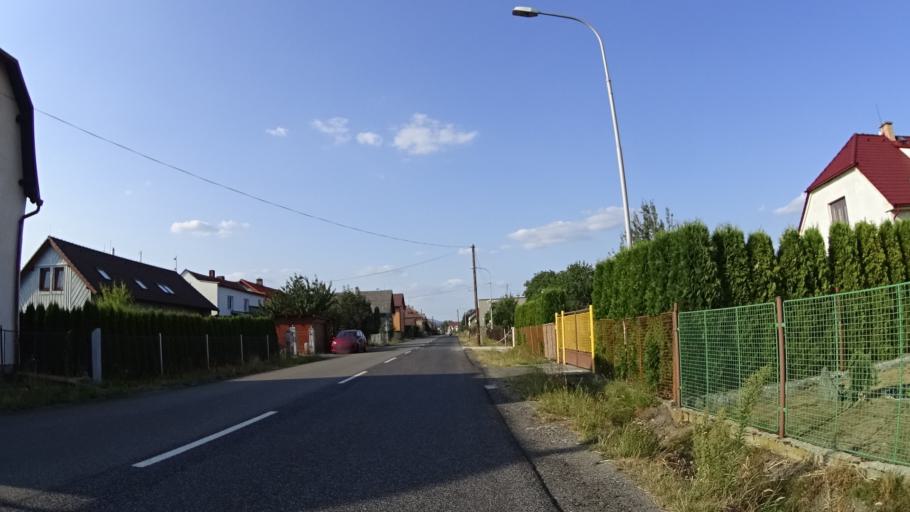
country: CZ
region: Central Bohemia
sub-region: Okres Mlada Boleslav
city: Zd'ar
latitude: 50.5528
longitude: 15.0678
